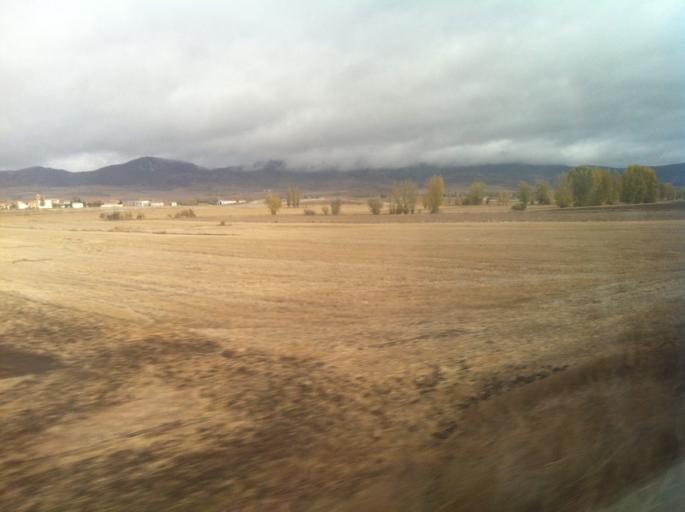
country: ES
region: Castille and Leon
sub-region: Provincia de Burgos
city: Fuentebureba
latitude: 42.6252
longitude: -3.2367
